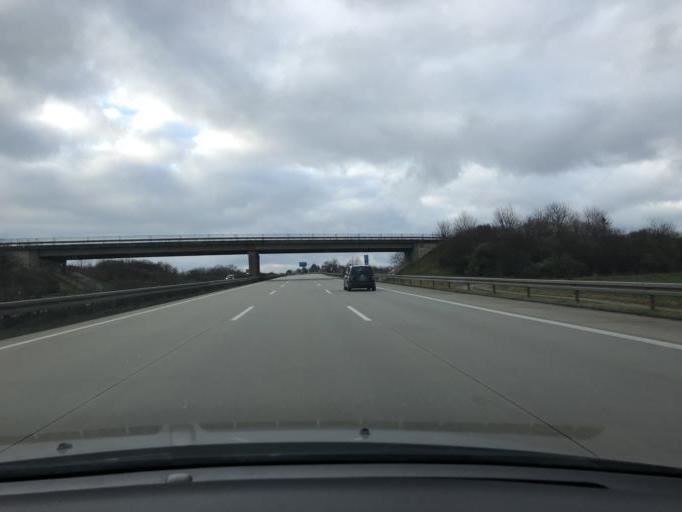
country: DE
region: Thuringia
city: Hartmannsdorf
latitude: 50.8977
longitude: 11.9803
